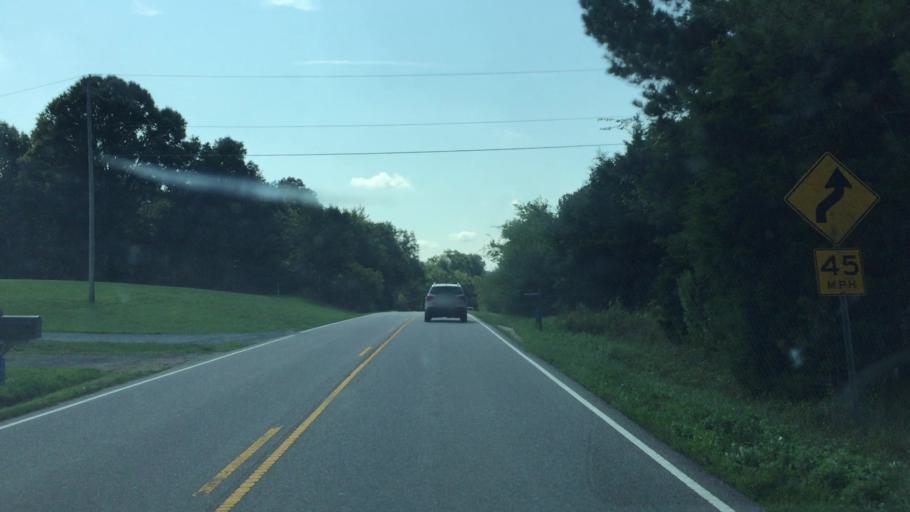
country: US
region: North Carolina
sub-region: Anson County
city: Burnsville
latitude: 35.1210
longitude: -80.3488
